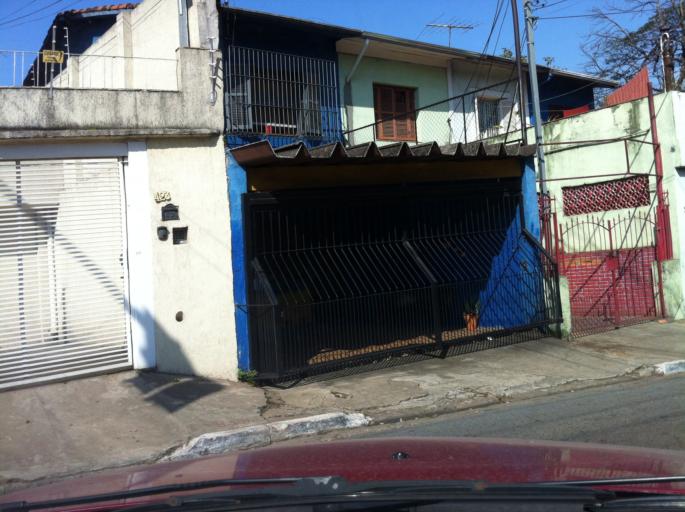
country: BR
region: Sao Paulo
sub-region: Diadema
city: Diadema
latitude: -23.6367
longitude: -46.6612
